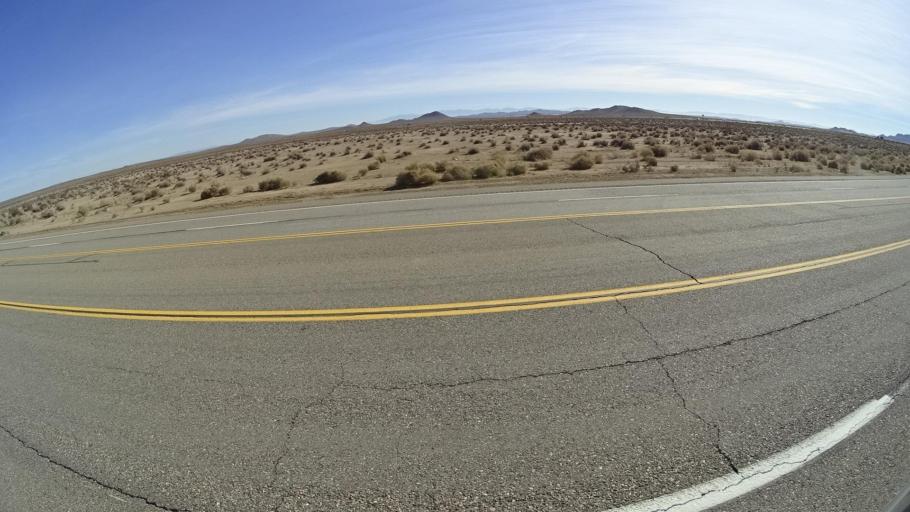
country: US
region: California
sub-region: Kern County
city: Mojave
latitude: 35.0389
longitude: -118.0975
